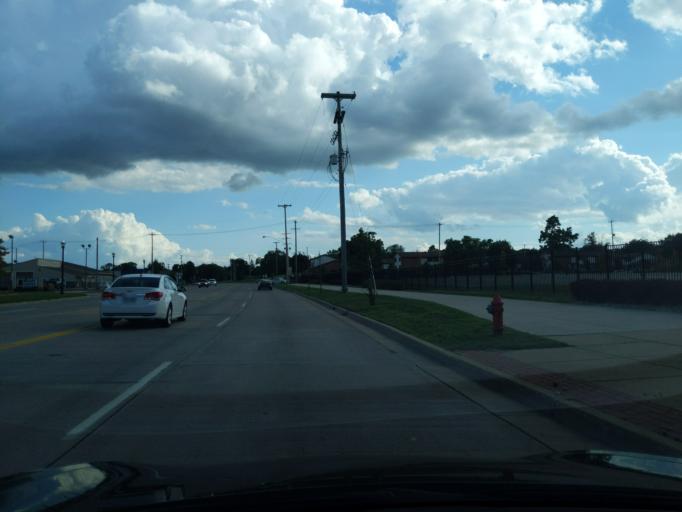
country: US
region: Michigan
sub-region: Jackson County
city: Jackson
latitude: 42.2452
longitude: -84.4005
